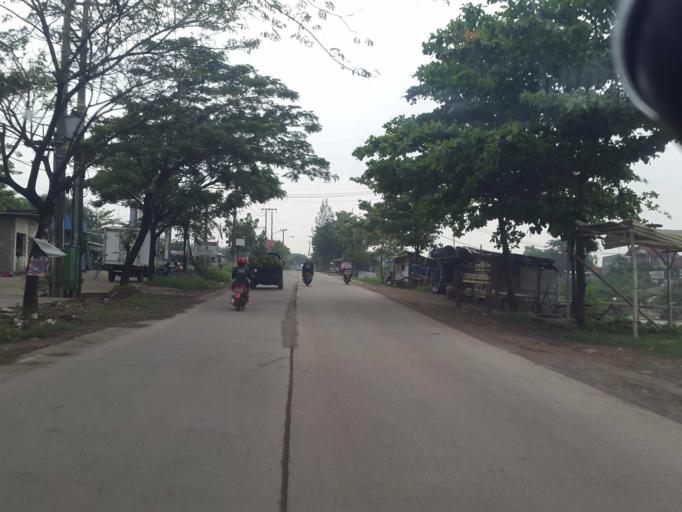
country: ID
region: West Java
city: Cikarang
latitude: -6.3238
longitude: 107.1677
